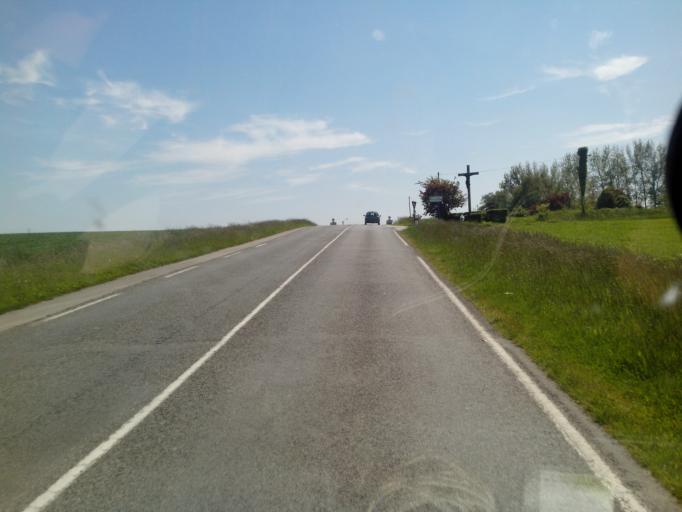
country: FR
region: Nord-Pas-de-Calais
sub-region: Departement du Pas-de-Calais
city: Samer
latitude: 50.6321
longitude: 1.7423
